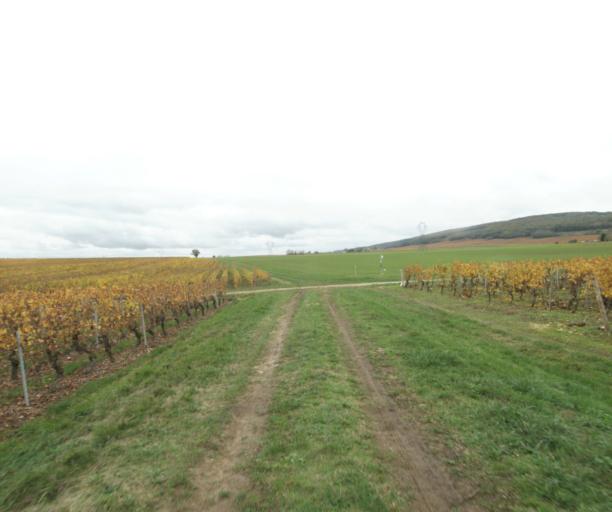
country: FR
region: Rhone-Alpes
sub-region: Departement de l'Ain
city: Pont-de-Vaux
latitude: 46.4712
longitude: 4.8613
